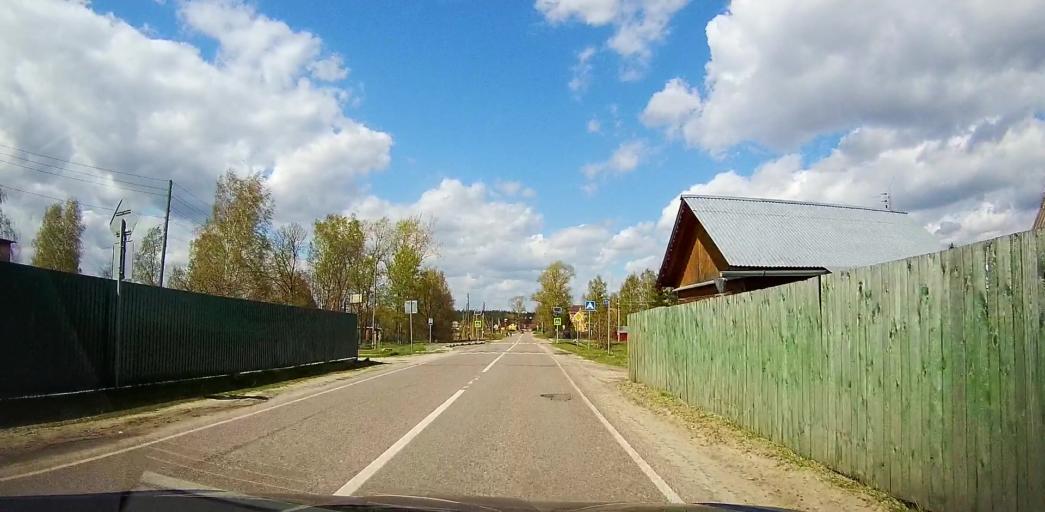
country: RU
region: Moskovskaya
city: Davydovo
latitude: 55.5558
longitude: 38.8147
